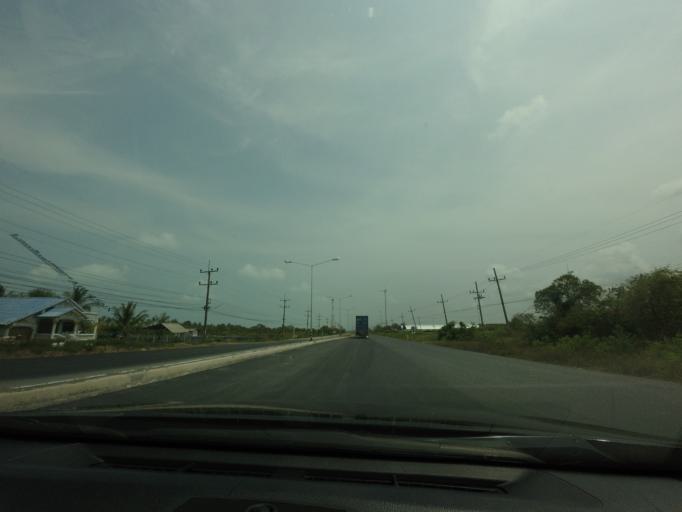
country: TH
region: Nakhon Si Thammarat
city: Hua Sai
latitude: 7.9222
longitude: 100.3354
